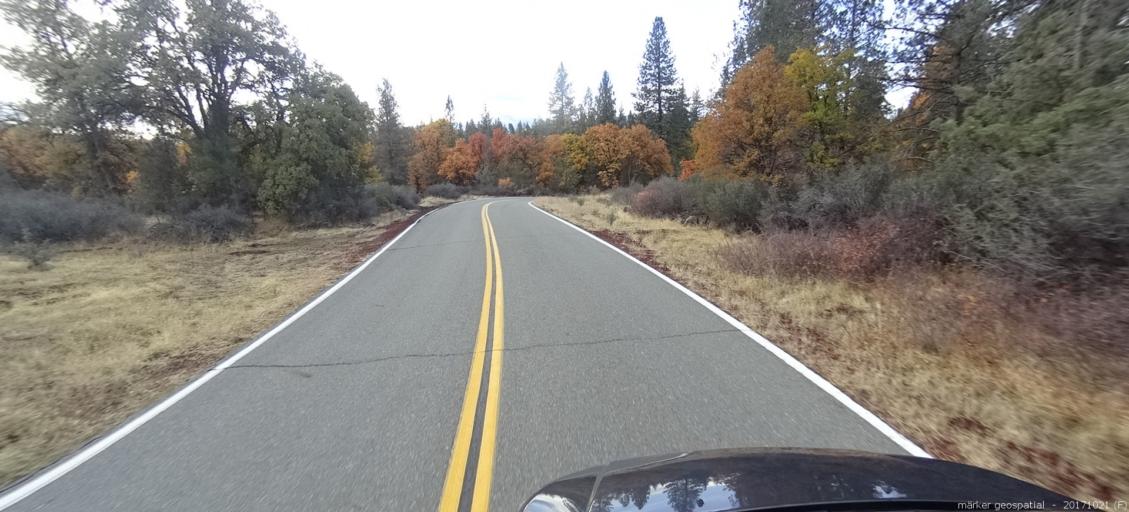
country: US
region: California
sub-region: Shasta County
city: Burney
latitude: 40.9214
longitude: -121.5338
